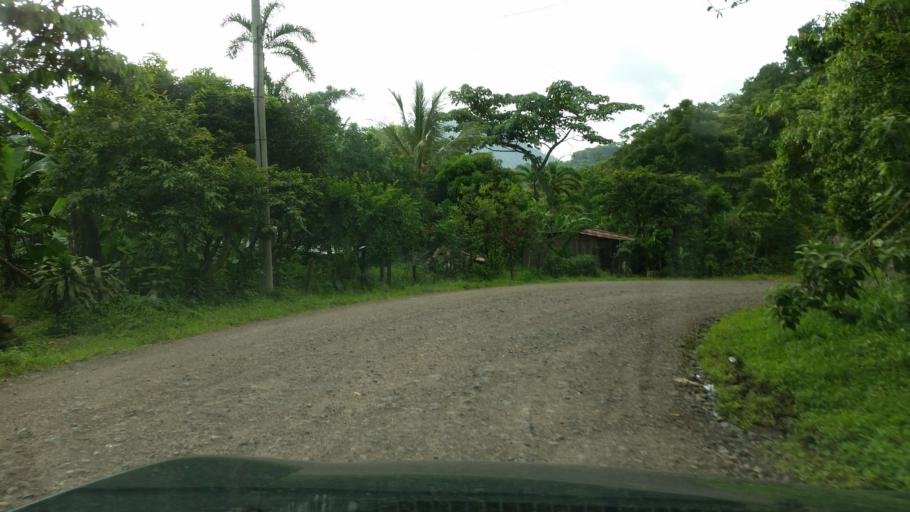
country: NI
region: Jinotega
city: Jinotega
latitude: 13.2439
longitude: -85.7295
